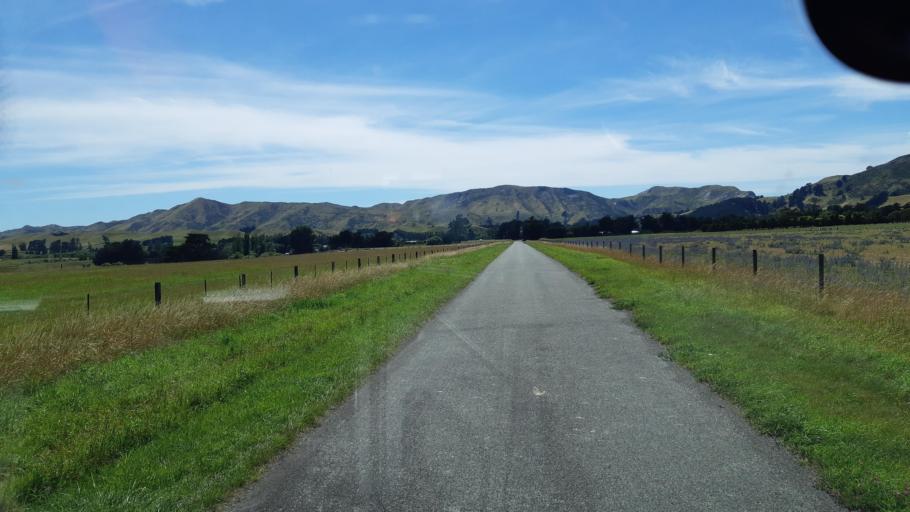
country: NZ
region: Marlborough
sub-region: Marlborough District
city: Blenheim
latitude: -41.8281
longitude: 174.1211
